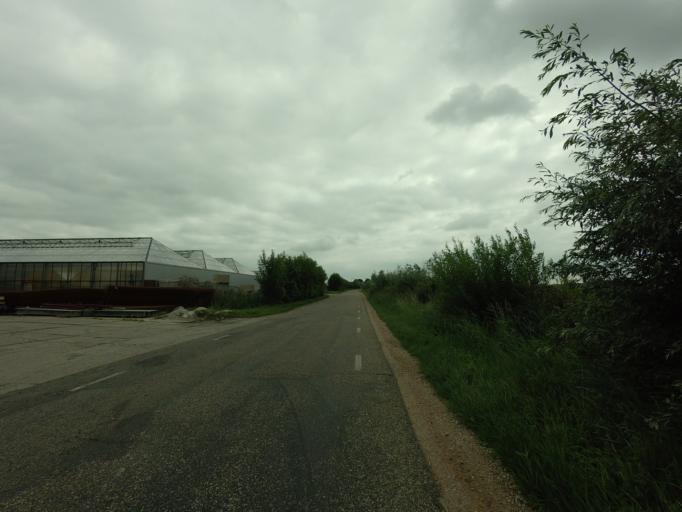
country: NL
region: Utrecht
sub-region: Gemeente De Ronde Venen
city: Mijdrecht
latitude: 52.2001
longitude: 4.9312
